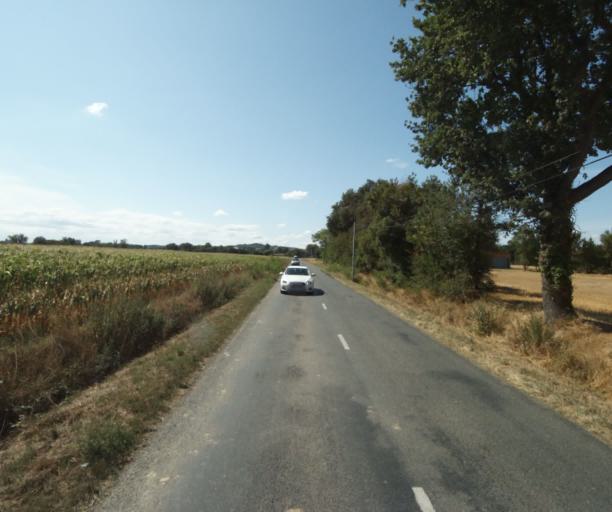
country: FR
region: Midi-Pyrenees
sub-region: Departement de la Haute-Garonne
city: Revel
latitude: 43.4898
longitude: 1.9803
